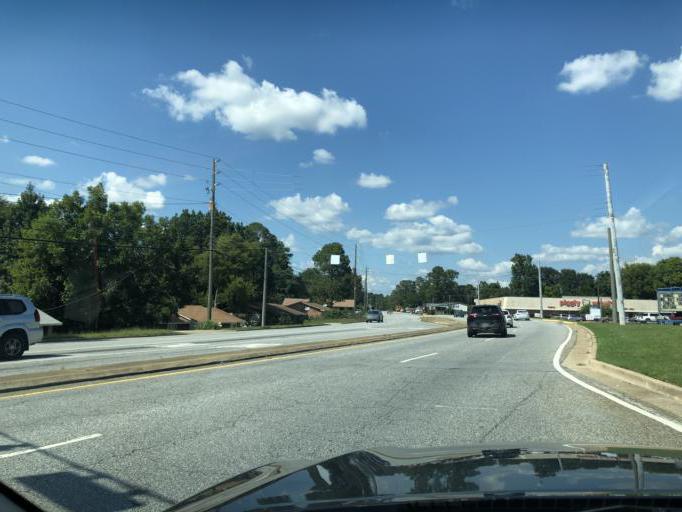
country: US
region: Georgia
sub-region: Muscogee County
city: Columbus
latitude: 32.5279
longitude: -84.9252
